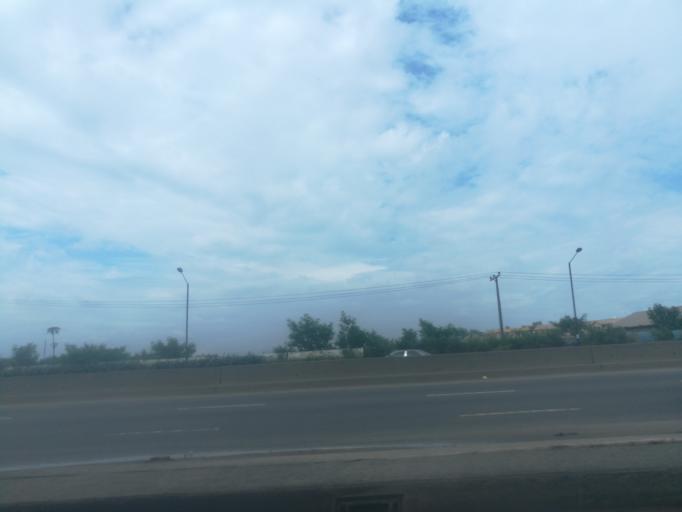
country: NG
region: Lagos
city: Somolu
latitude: 6.5542
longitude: 3.3730
